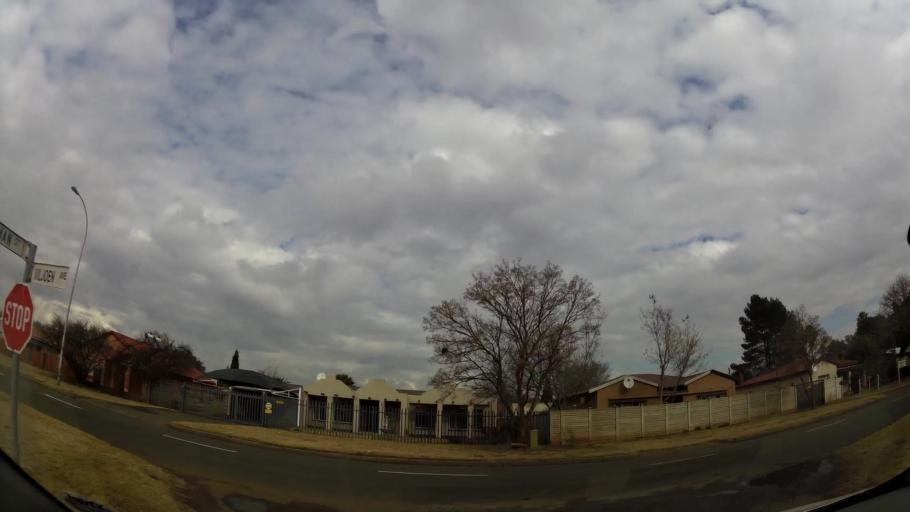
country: ZA
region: Gauteng
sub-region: Sedibeng District Municipality
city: Meyerton
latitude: -26.6013
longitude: 27.9960
